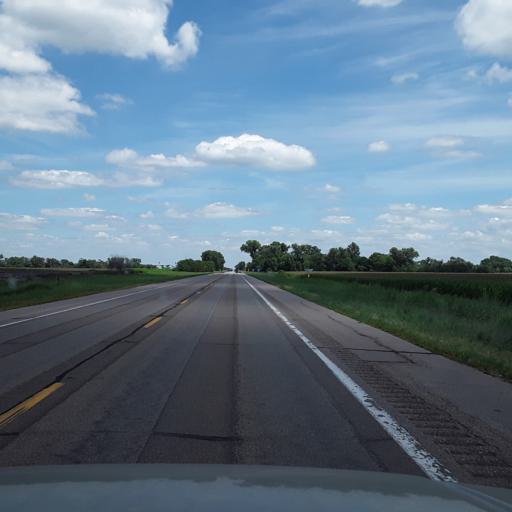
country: US
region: Nebraska
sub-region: Polk County
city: Osceola
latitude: 41.3484
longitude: -97.5868
